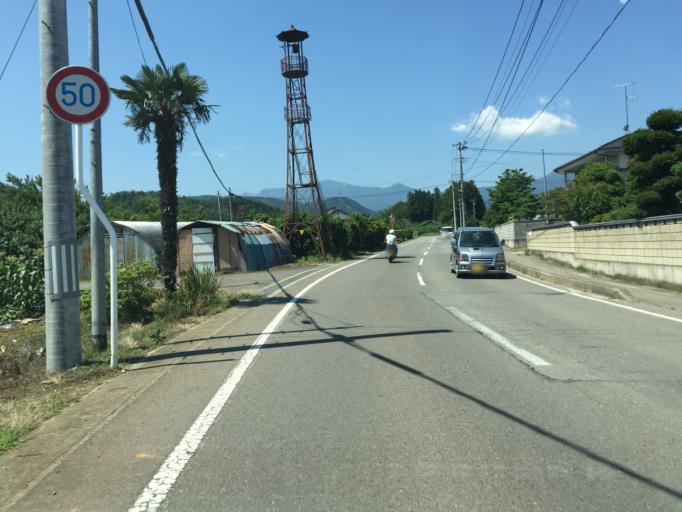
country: JP
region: Fukushima
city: Fukushima-shi
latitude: 37.7198
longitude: 140.3992
